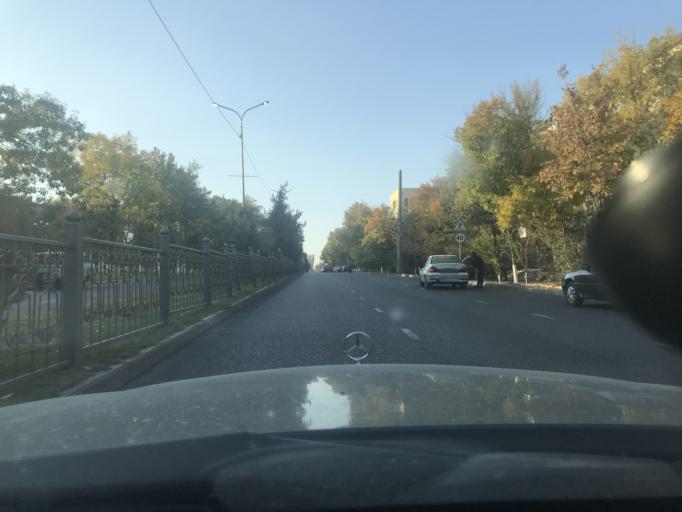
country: KZ
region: Ongtustik Qazaqstan
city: Shymkent
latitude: 42.3023
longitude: 69.6053
